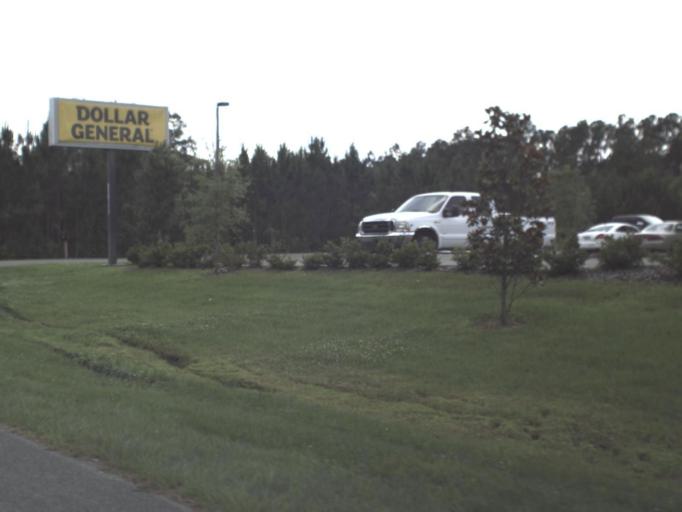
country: US
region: Florida
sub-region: Nassau County
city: Yulee
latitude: 30.6260
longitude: -81.5996
